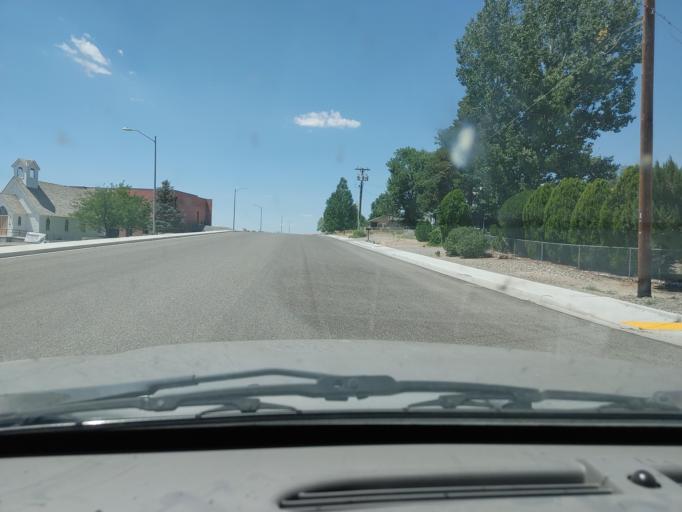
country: US
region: Nevada
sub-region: Humboldt County
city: Winnemucca
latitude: 40.9778
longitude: -117.7430
